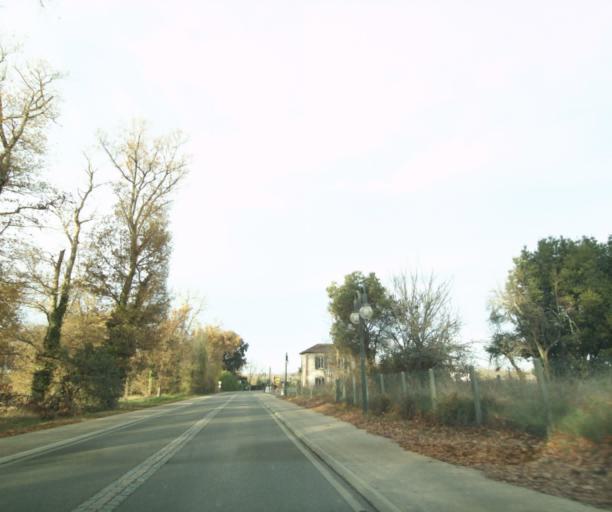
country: FR
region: Midi-Pyrenees
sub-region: Departement du Gers
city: Cazaubon
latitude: 43.9353
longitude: -0.0598
